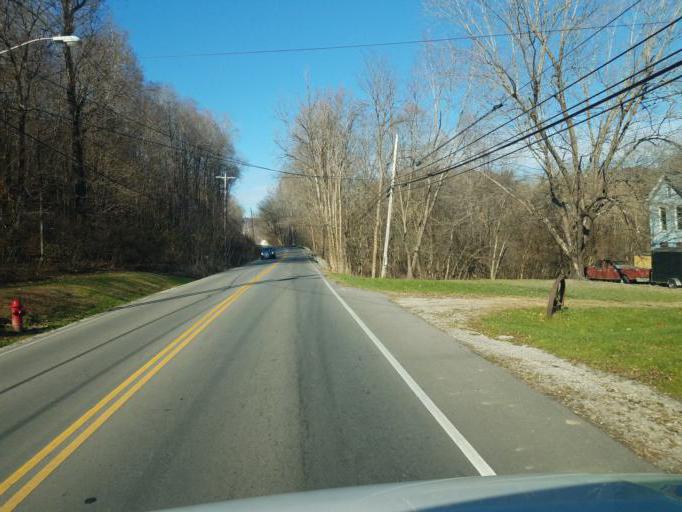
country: US
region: Ohio
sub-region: Scioto County
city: New Boston
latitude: 38.7713
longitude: -82.9398
